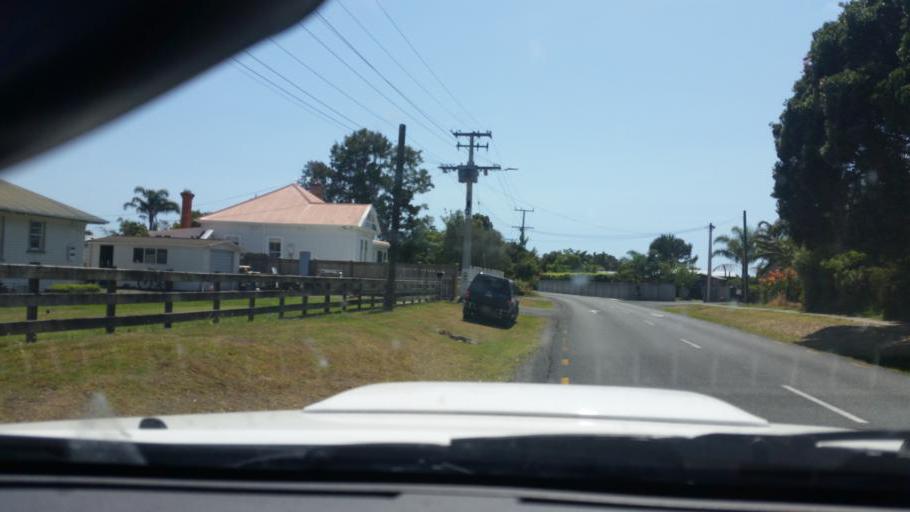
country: NZ
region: Auckland
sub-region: Auckland
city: Wellsford
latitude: -36.1251
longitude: 174.5780
